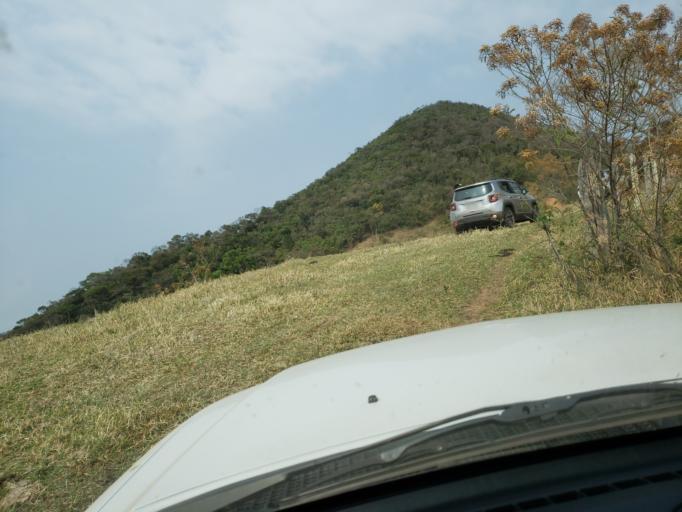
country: BR
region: Minas Gerais
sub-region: Jacutinga
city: Jacutinga
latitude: -22.3443
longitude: -46.5874
